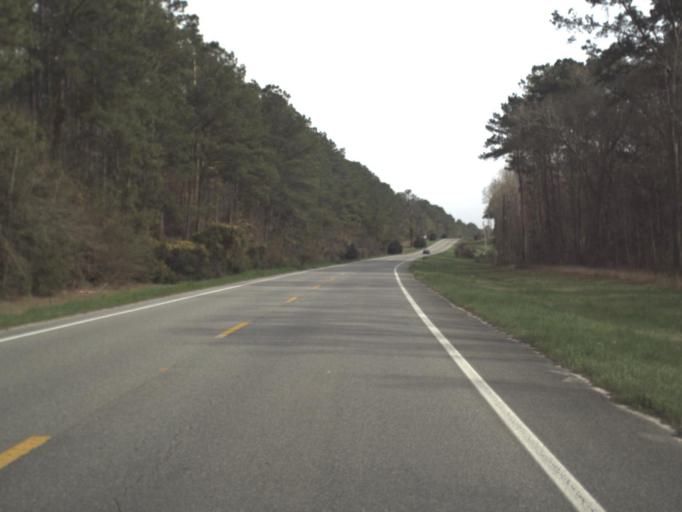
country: US
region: Florida
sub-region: Jefferson County
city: Monticello
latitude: 30.5419
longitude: -83.8403
